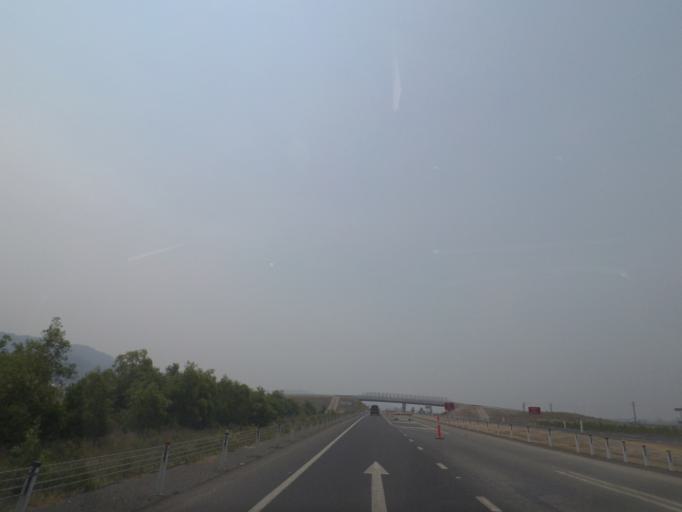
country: AU
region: New South Wales
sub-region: Ballina
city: Ballina
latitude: -28.9043
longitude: 153.4791
